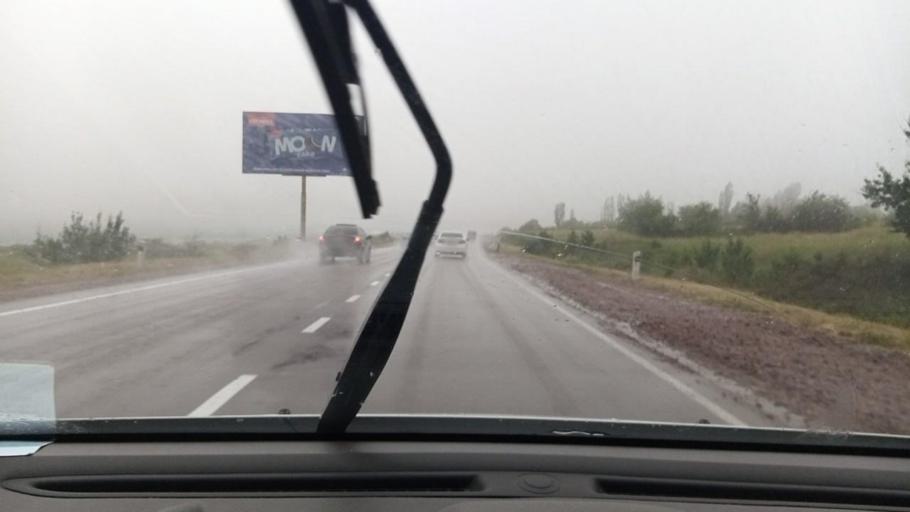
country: UZ
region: Toshkent
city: Angren
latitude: 41.0497
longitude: 70.1579
